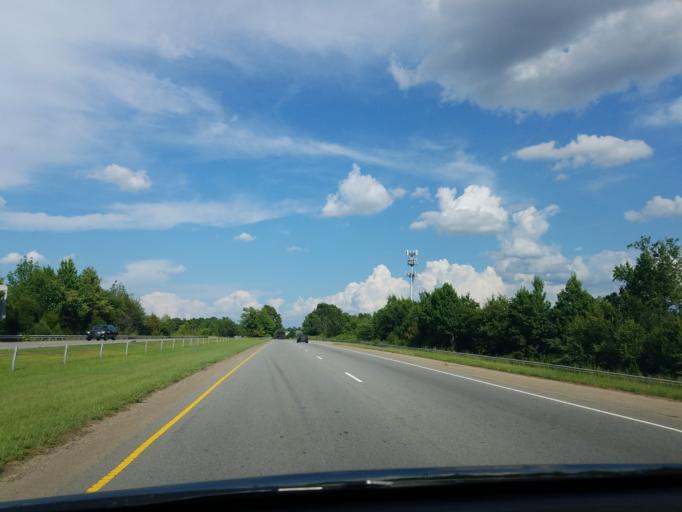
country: US
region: North Carolina
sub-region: Wake County
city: Apex
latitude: 35.7495
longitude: -78.8502
